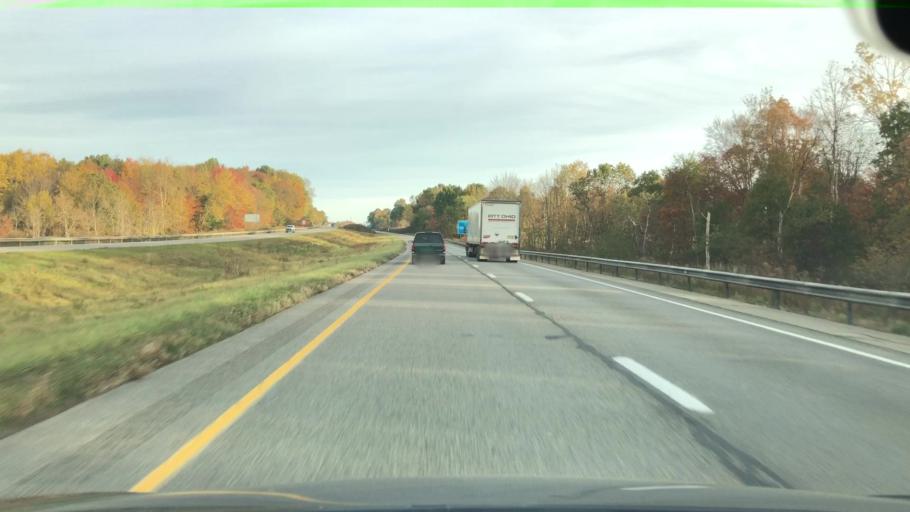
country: US
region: Pennsylvania
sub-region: Mercer County
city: Stoneboro
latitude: 41.3702
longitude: -80.1570
